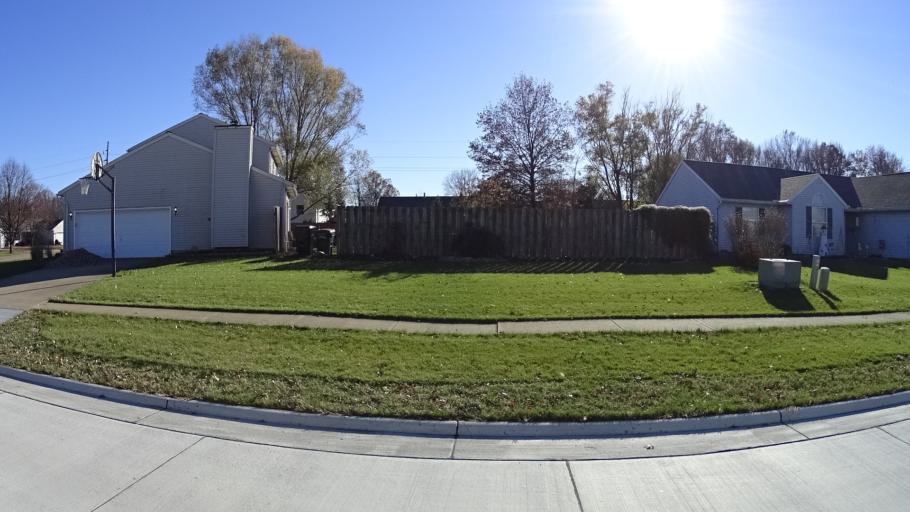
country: US
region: Ohio
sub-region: Lorain County
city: Elyria
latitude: 41.3503
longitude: -82.0800
